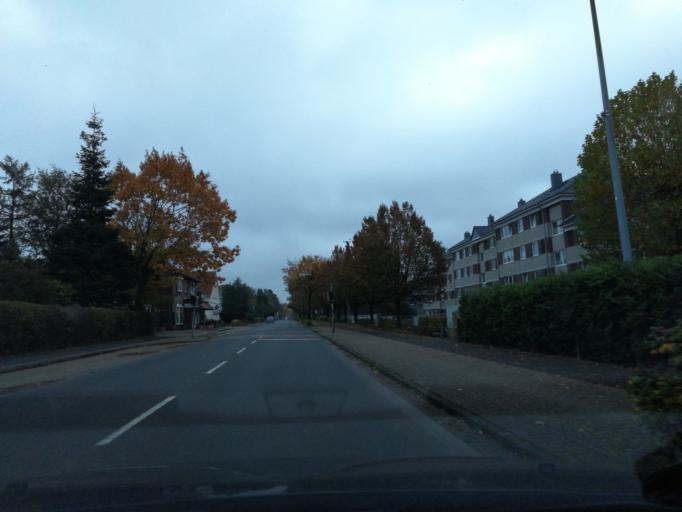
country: DE
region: Lower Saxony
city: Schortens
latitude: 53.5442
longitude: 7.9397
